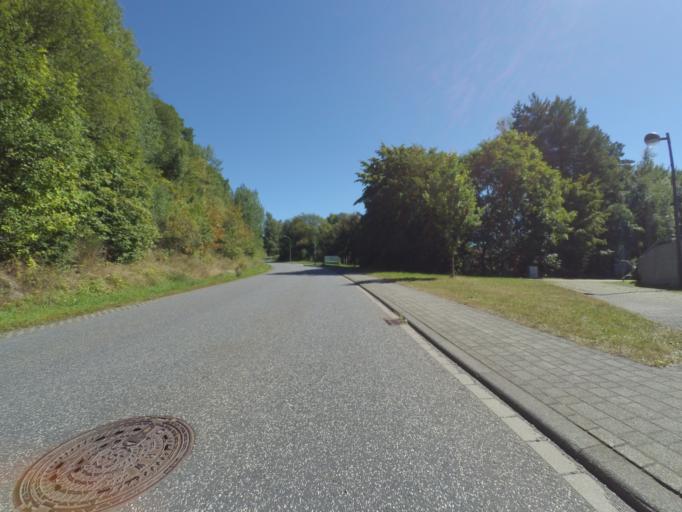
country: DE
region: Rheinland-Pfalz
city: Junkerath
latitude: 50.3423
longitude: 6.5872
